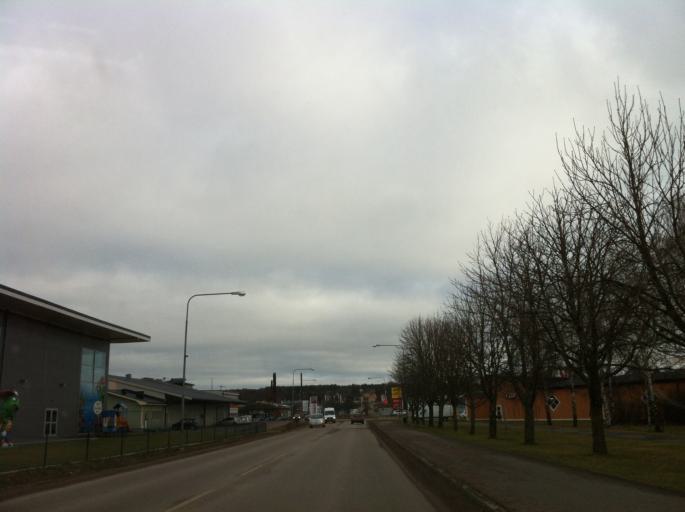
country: SE
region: Kalmar
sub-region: Vimmerby Kommun
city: Vimmerby
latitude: 57.6656
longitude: 15.8405
